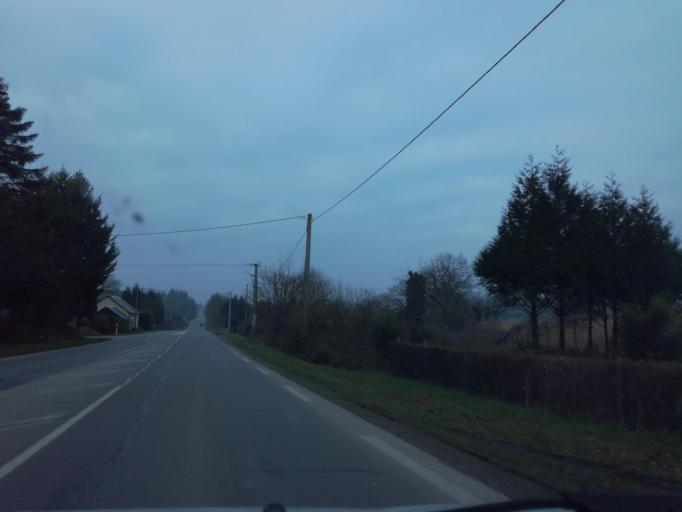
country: FR
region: Brittany
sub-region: Departement d'Ille-et-Vilaine
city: Gosne
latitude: 48.2278
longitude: -1.4807
